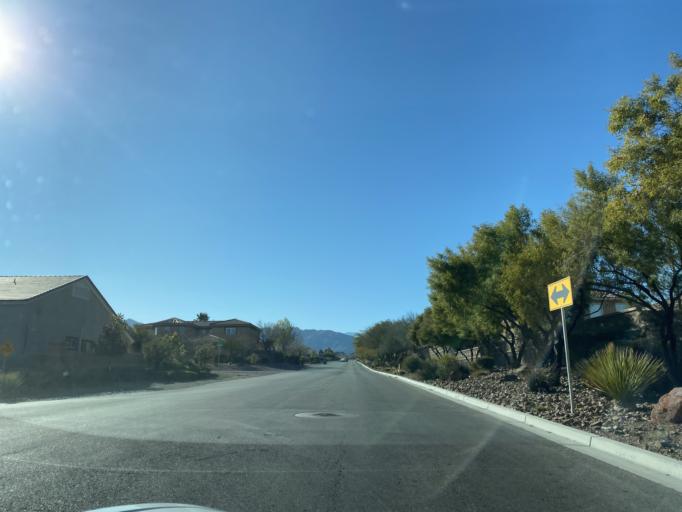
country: US
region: Nevada
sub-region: Clark County
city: Summerlin South
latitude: 36.2957
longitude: -115.3073
